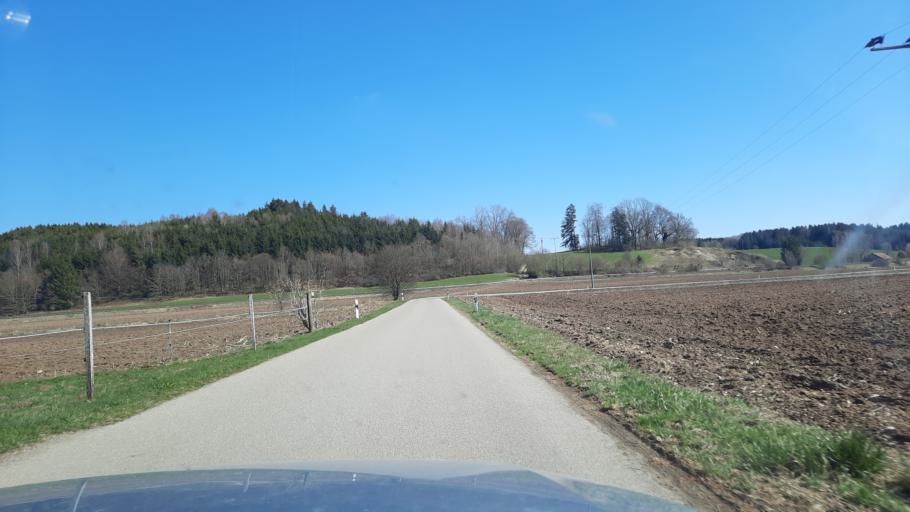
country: DE
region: Bavaria
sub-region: Swabia
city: Wolfertschwenden
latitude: 47.8541
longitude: 10.2526
